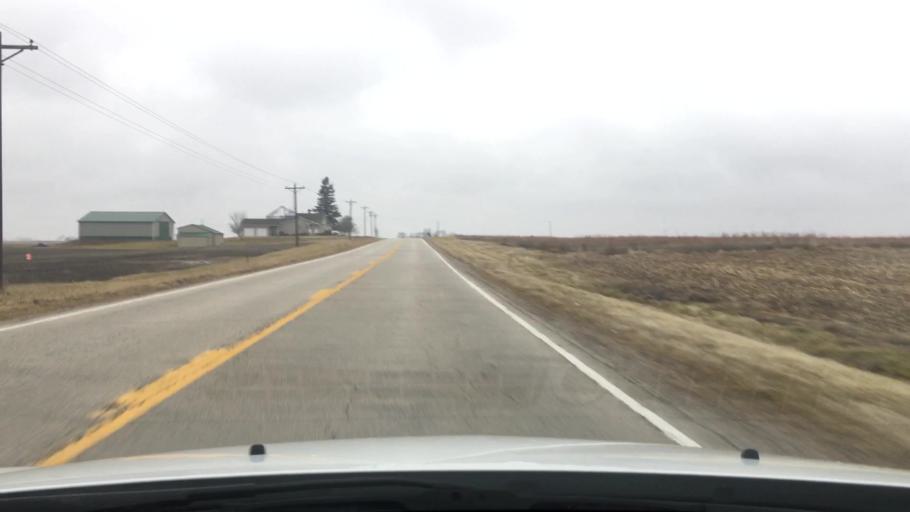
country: US
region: Illinois
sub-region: Iroquois County
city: Watseka
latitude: 40.8905
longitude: -87.7075
